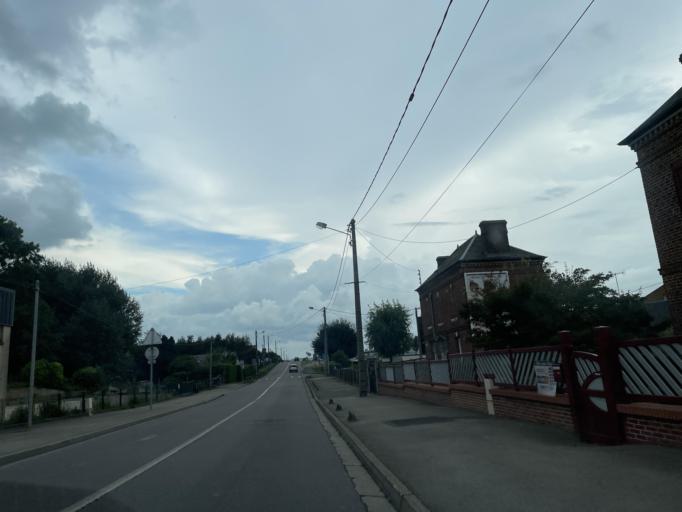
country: FR
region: Haute-Normandie
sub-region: Departement de la Seine-Maritime
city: Gournay-en-Bray
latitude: 49.4806
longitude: 1.7381
